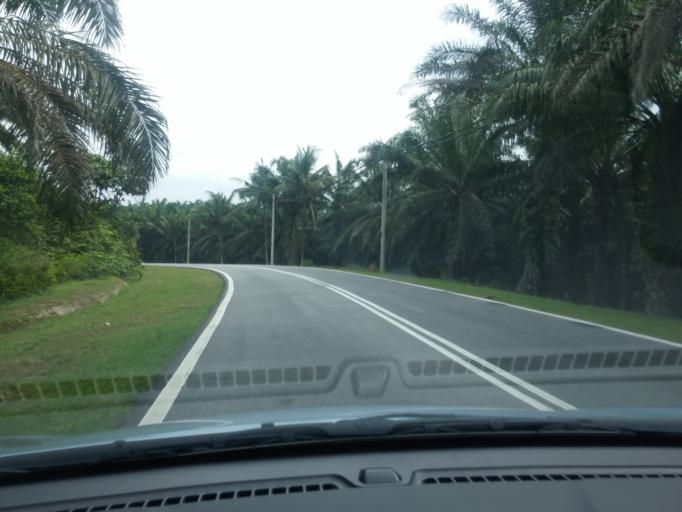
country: MY
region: Pahang
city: Kuantan
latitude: 3.8600
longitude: 103.1644
